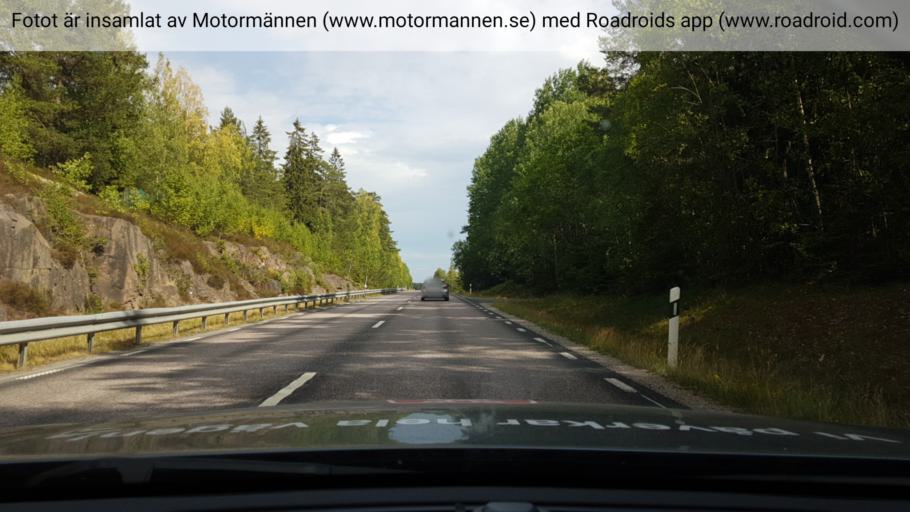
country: SE
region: Uppsala
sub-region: Enkopings Kommun
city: Orsundsbro
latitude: 59.8676
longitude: 17.3250
